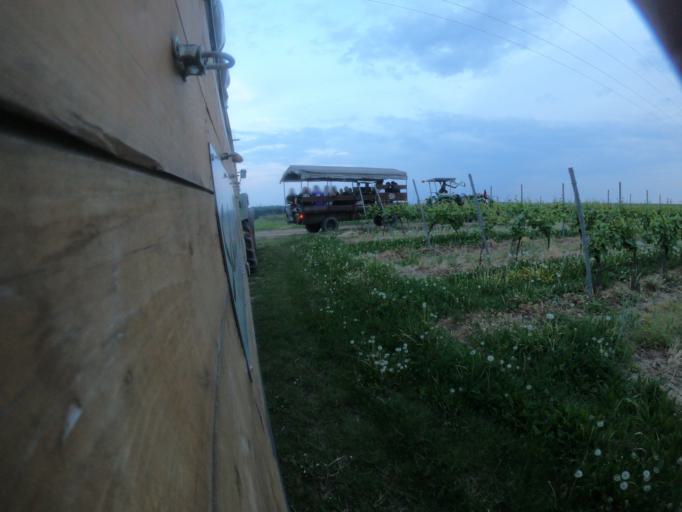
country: DE
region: Rheinland-Pfalz
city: Dalheim
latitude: 49.8213
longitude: 8.2892
